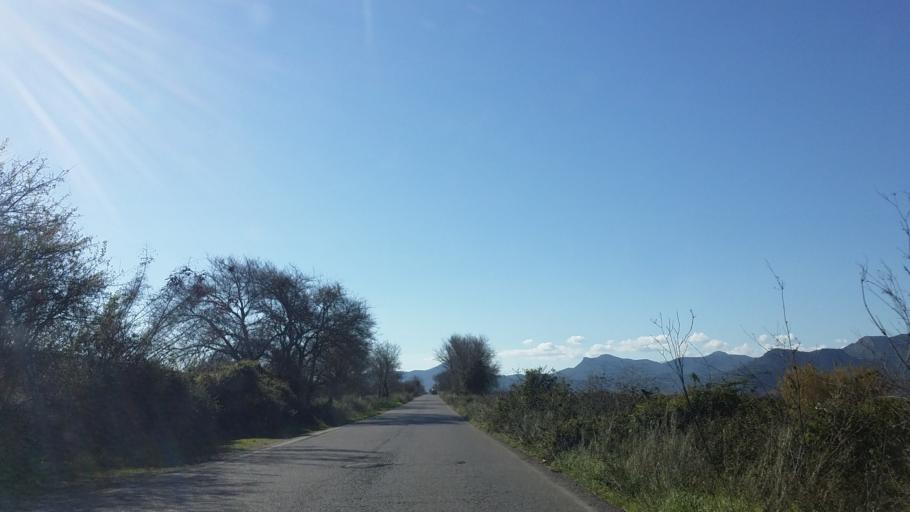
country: GR
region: West Greece
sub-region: Nomos Aitolias kai Akarnanias
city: Vonitsa
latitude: 38.8588
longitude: 20.8765
